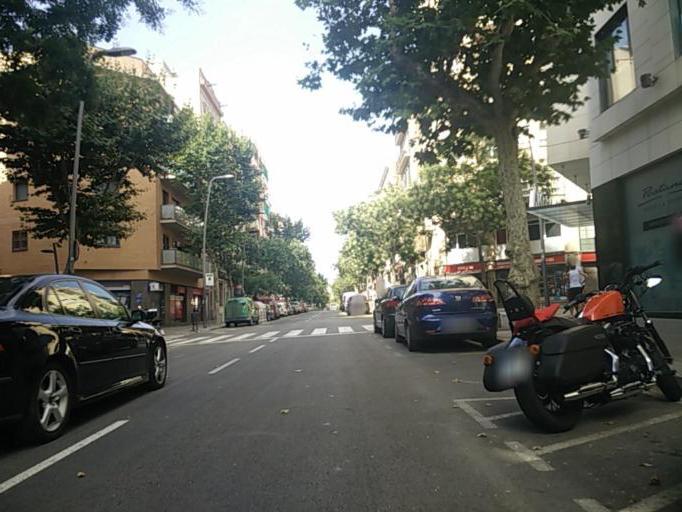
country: ES
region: Catalonia
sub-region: Provincia de Barcelona
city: Sants-Montjuic
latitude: 41.3767
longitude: 2.1463
